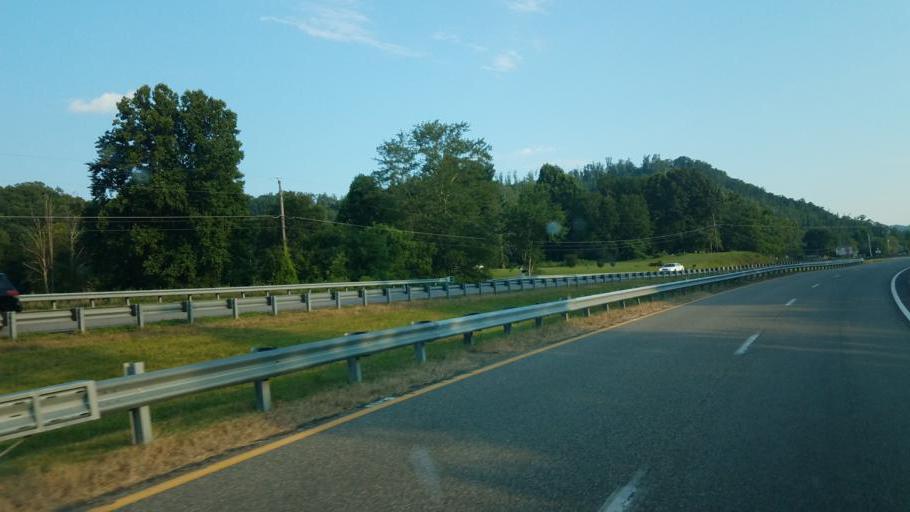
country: US
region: Virginia
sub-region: Lee County
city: Dryden
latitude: 36.7333
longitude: -82.7958
